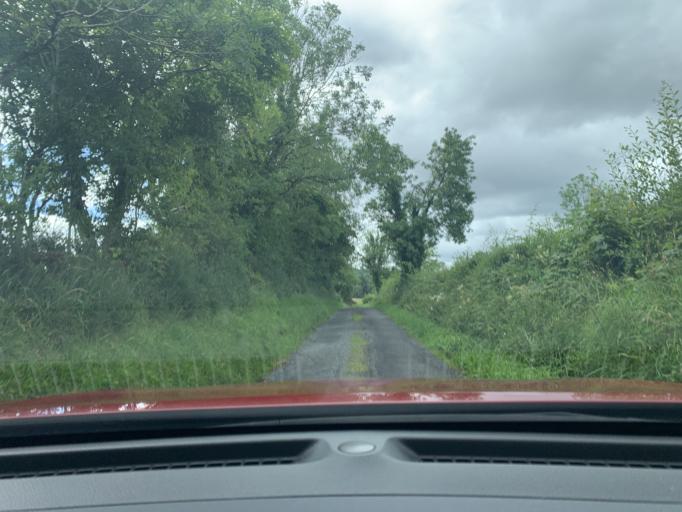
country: GB
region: Northern Ireland
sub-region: Fermanagh District
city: Enniskillen
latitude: 54.2761
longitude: -7.8065
